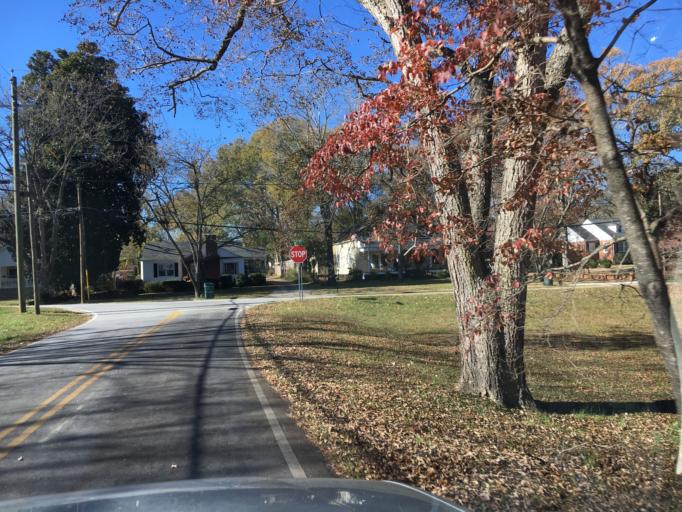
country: US
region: Georgia
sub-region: Hart County
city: Hartwell
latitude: 34.3468
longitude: -82.9421
